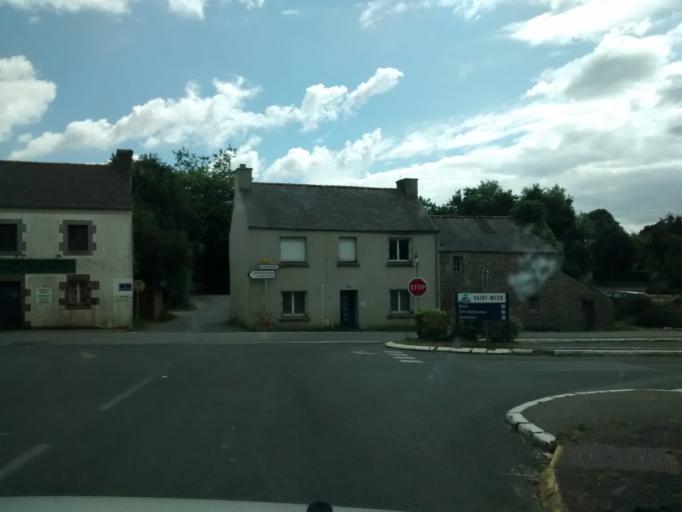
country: FR
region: Brittany
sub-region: Departement du Finistere
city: Lesneven
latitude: 48.5598
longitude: -4.2631
